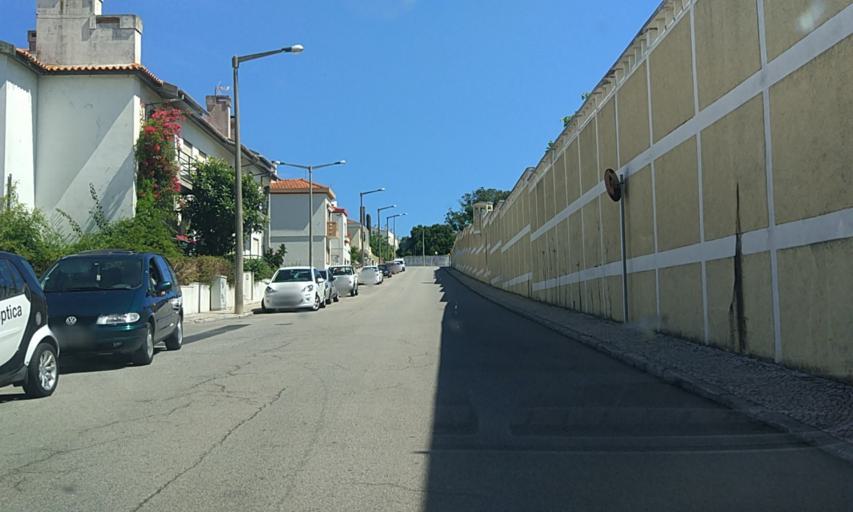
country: PT
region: Coimbra
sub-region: Figueira da Foz
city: Figueira da Foz
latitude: 40.1528
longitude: -8.8529
